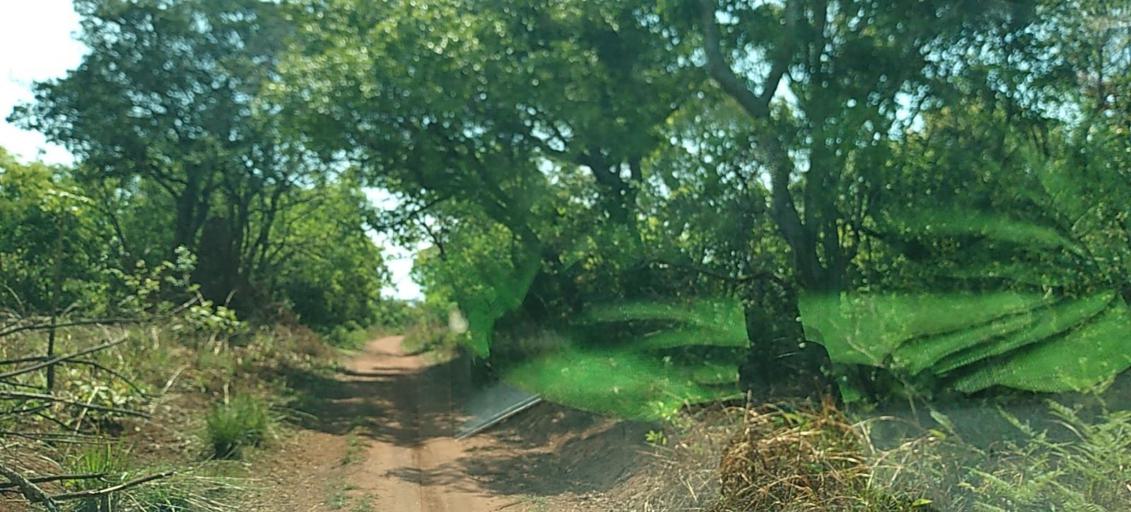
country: CD
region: Katanga
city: Kolwezi
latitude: -11.2816
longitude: 25.1387
